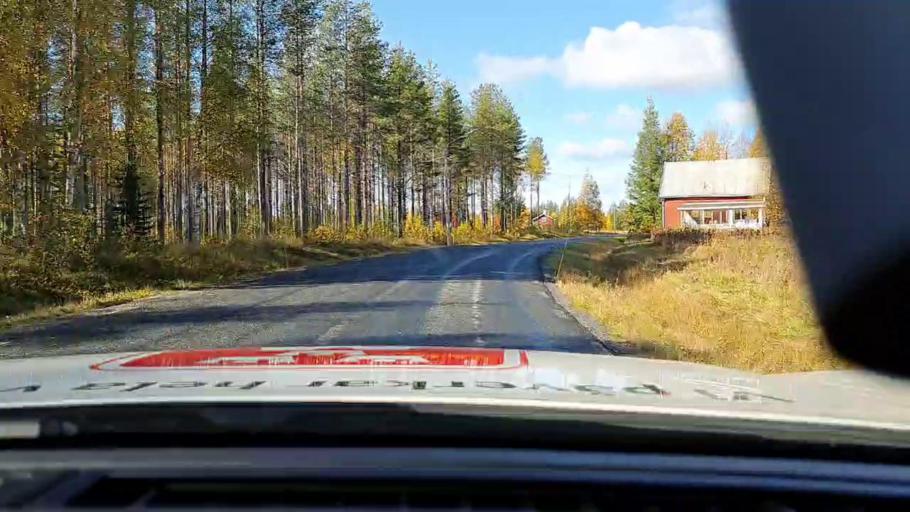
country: SE
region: Vaesterbotten
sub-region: Skelleftea Kommun
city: Langsele
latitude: 65.0112
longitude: 20.0842
